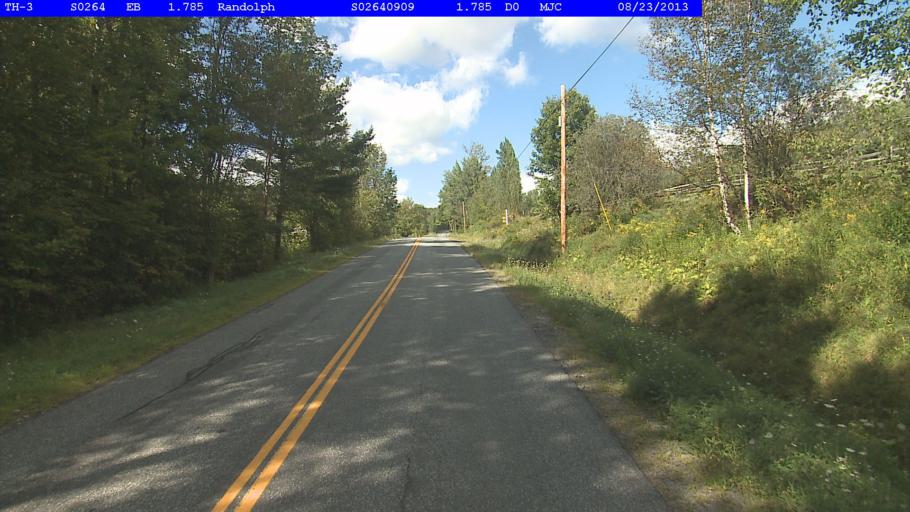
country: US
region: Vermont
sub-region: Orange County
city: Chelsea
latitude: 43.9524
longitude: -72.5329
